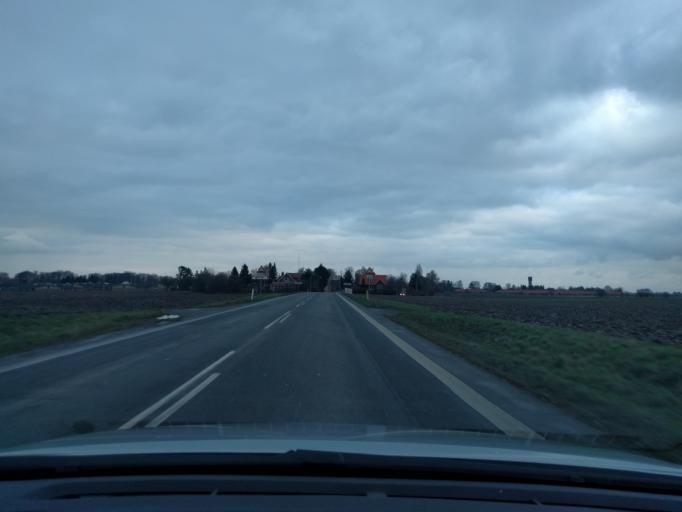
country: DK
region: Zealand
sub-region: Guldborgsund Kommune
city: Stubbekobing
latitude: 54.8812
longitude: 12.0318
